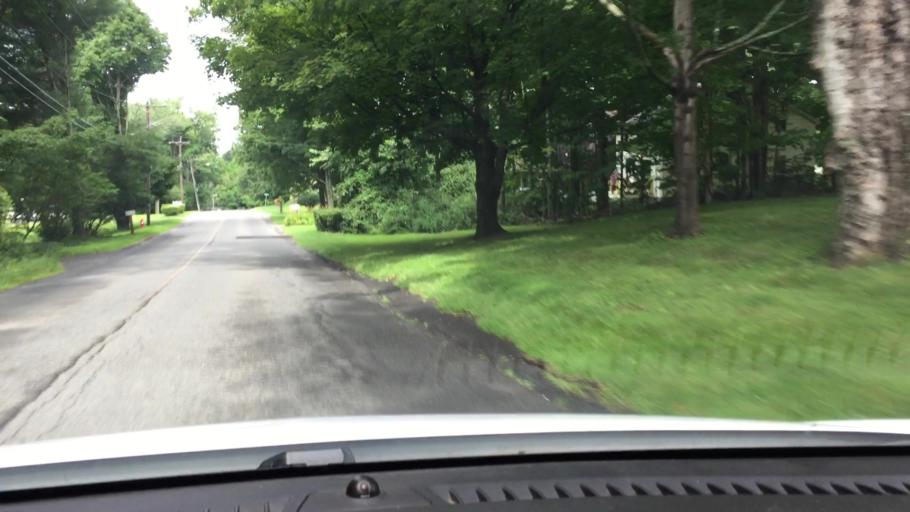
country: US
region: Massachusetts
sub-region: Berkshire County
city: Dalton
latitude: 42.4608
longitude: -73.1776
